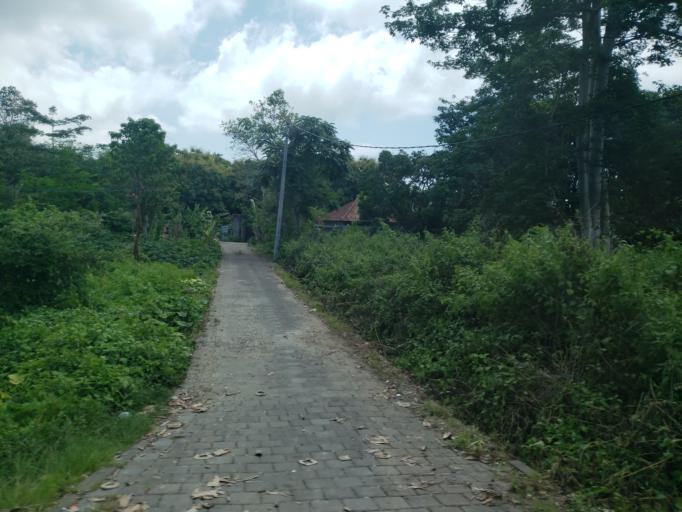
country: ID
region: Bali
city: Kangin
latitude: -8.8269
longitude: 115.1501
